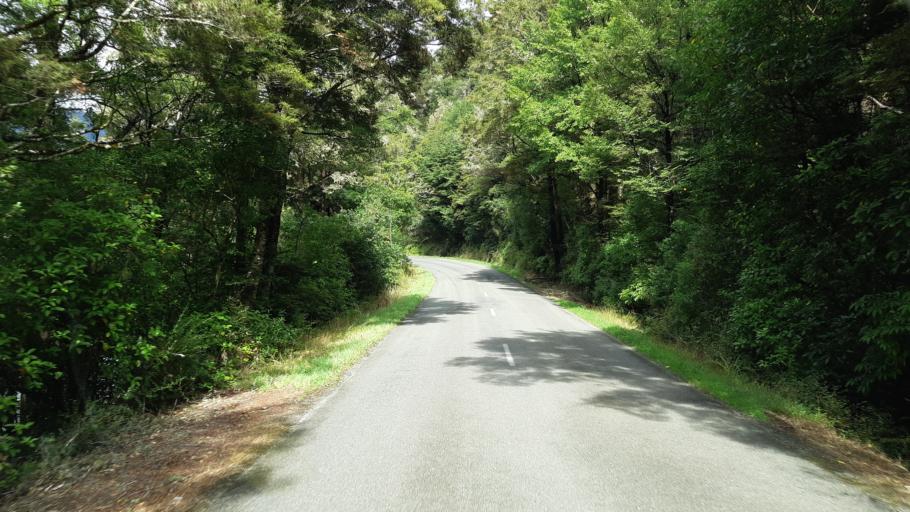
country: NZ
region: West Coast
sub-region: Buller District
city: Westport
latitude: -41.7845
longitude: 172.3684
